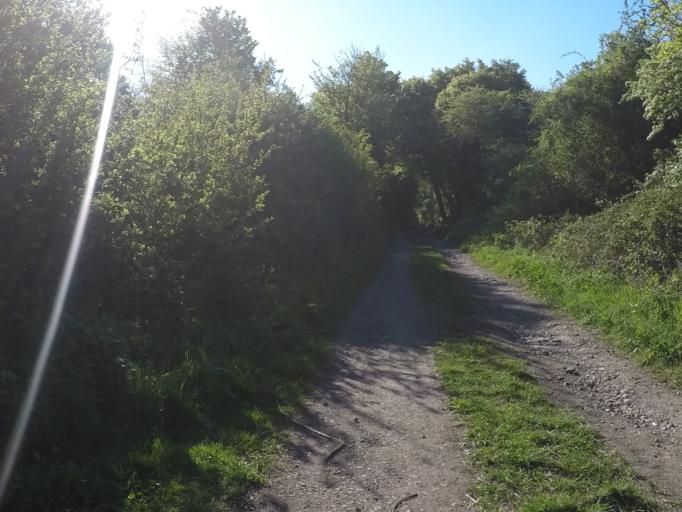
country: GB
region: England
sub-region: Oxfordshire
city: Charlbury
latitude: 51.8747
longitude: -1.4673
